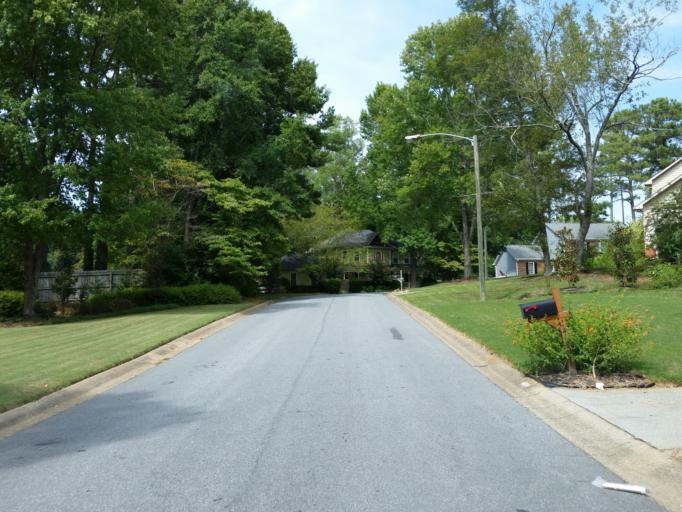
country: US
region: Georgia
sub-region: Cherokee County
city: Woodstock
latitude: 34.0288
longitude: -84.5118
